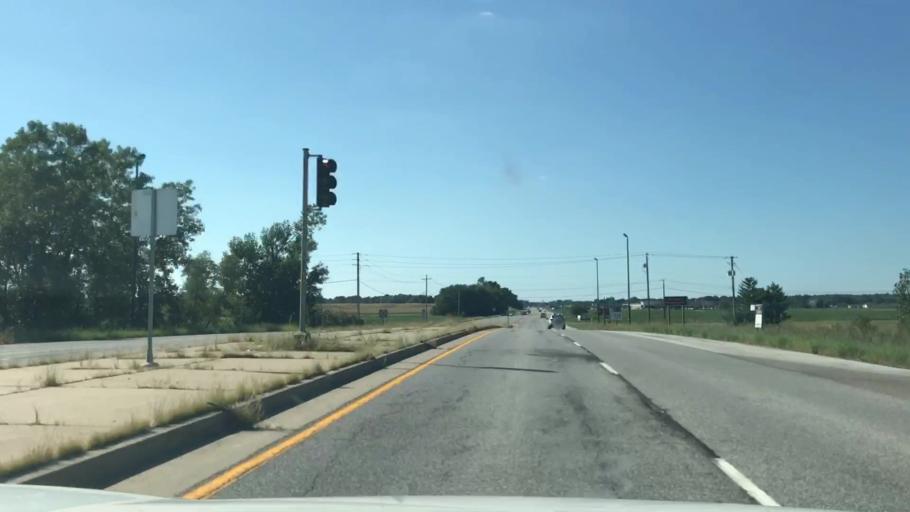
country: US
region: Illinois
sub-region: Madison County
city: Roxana
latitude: 38.8515
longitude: -90.0539
